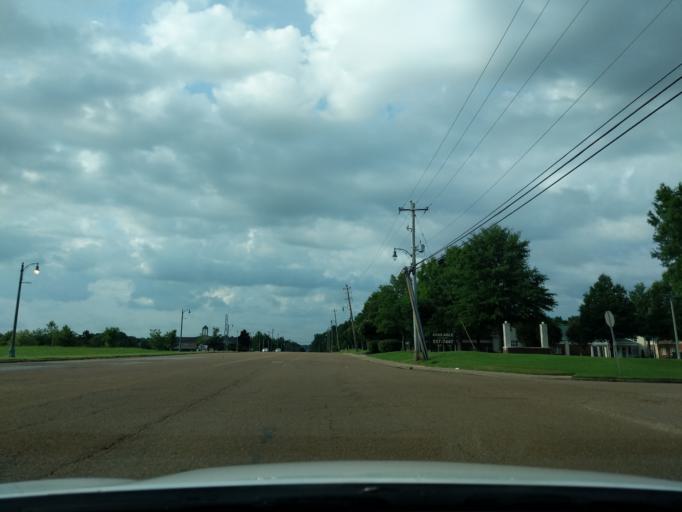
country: US
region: Tennessee
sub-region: Shelby County
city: Germantown
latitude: 35.0447
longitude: -89.7599
